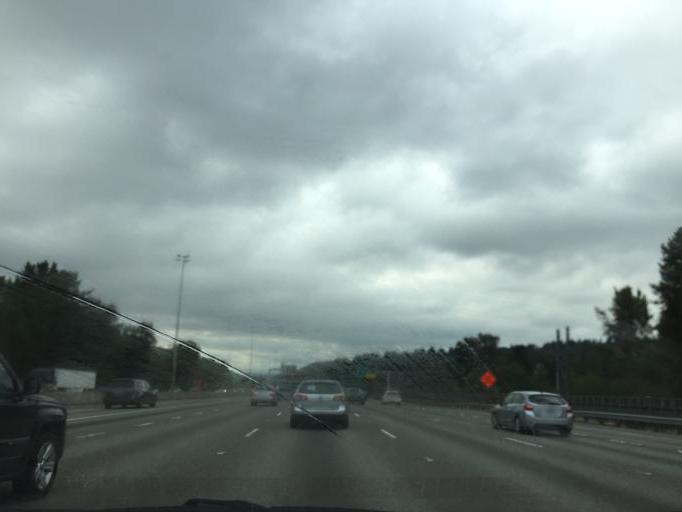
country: US
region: Washington
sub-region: King County
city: Tukwila
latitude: 47.4720
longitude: -122.2691
